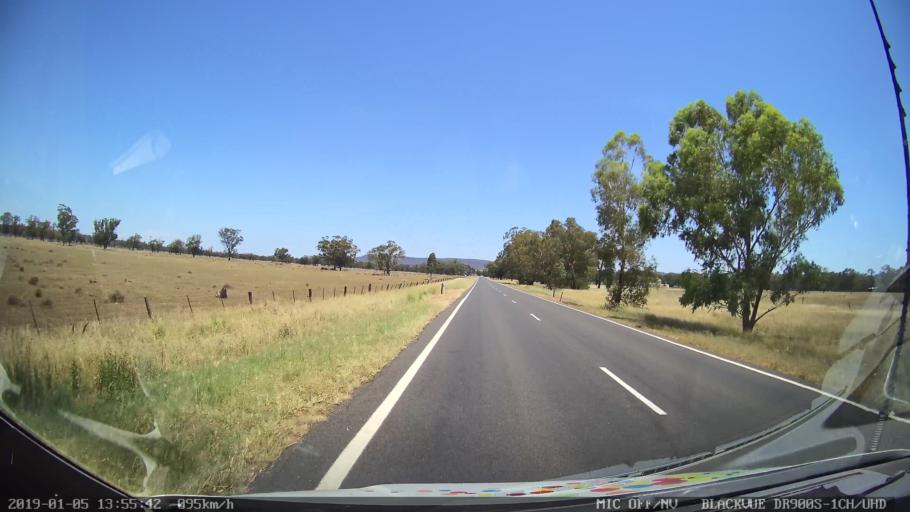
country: AU
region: New South Wales
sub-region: Gunnedah
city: Gunnedah
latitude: -31.1066
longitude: 150.2697
